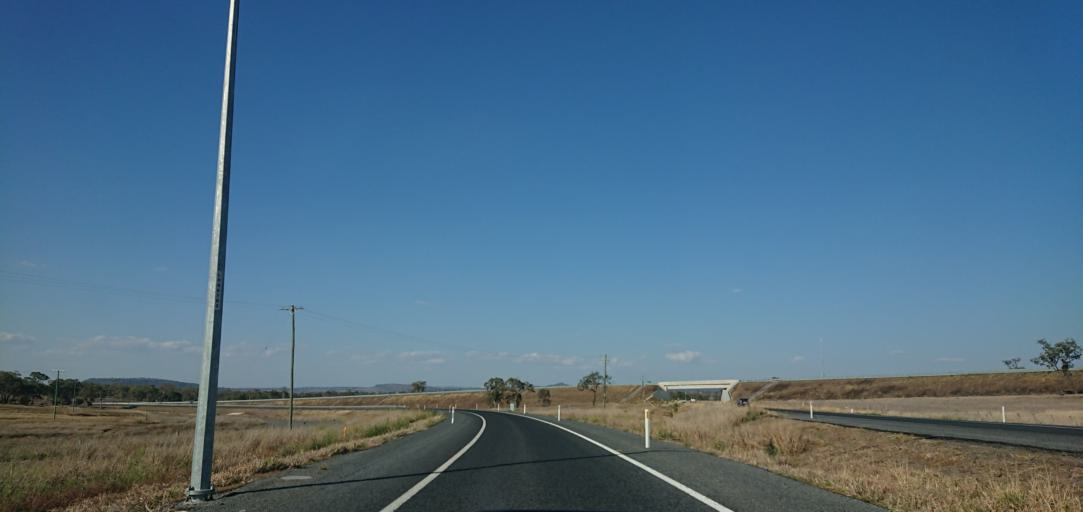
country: AU
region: Queensland
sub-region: Toowoomba
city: Westbrook
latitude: -27.6158
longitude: 151.7826
